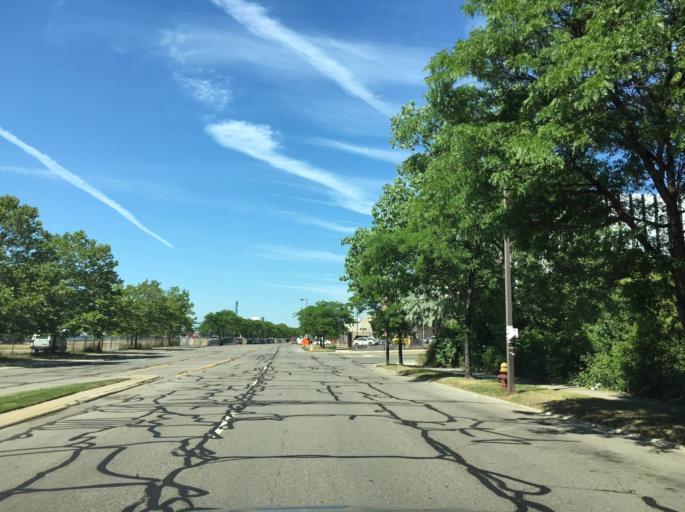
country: US
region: Michigan
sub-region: Wayne County
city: Detroit
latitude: 42.3247
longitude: -83.0579
